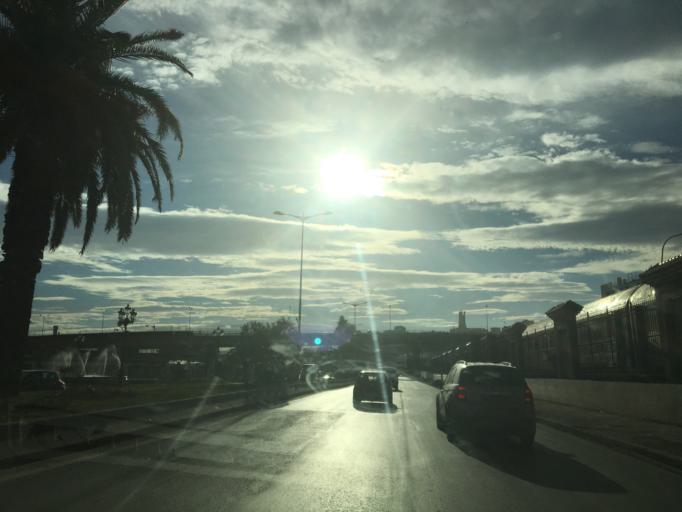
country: DZ
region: Alger
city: Algiers
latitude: 36.7629
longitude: 3.0588
